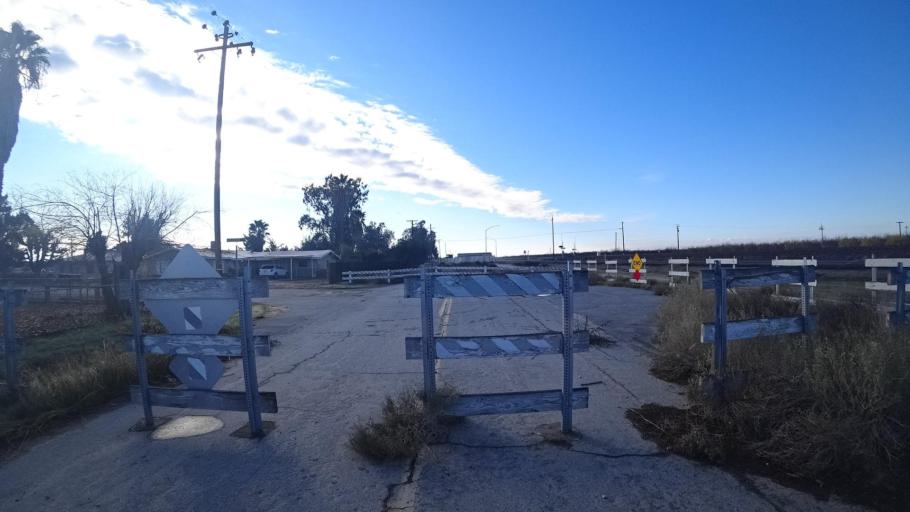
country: US
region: California
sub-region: Kern County
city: Delano
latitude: 35.7188
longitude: -119.3303
